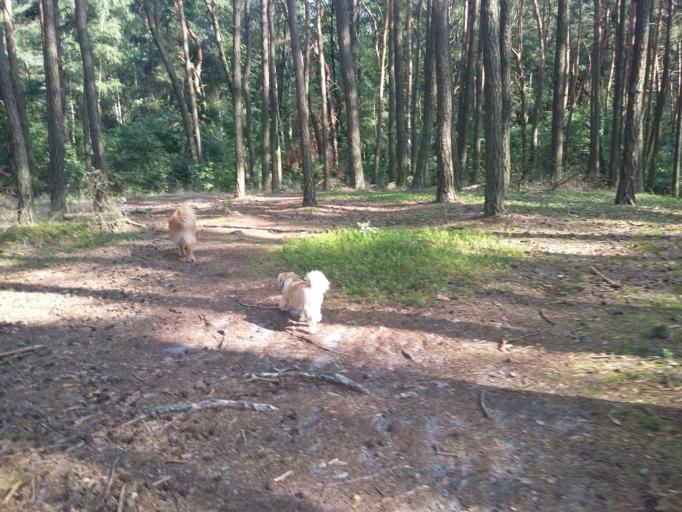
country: PL
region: Lodz Voivodeship
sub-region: Powiat pabianicki
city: Dobron
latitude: 51.5905
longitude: 19.2253
